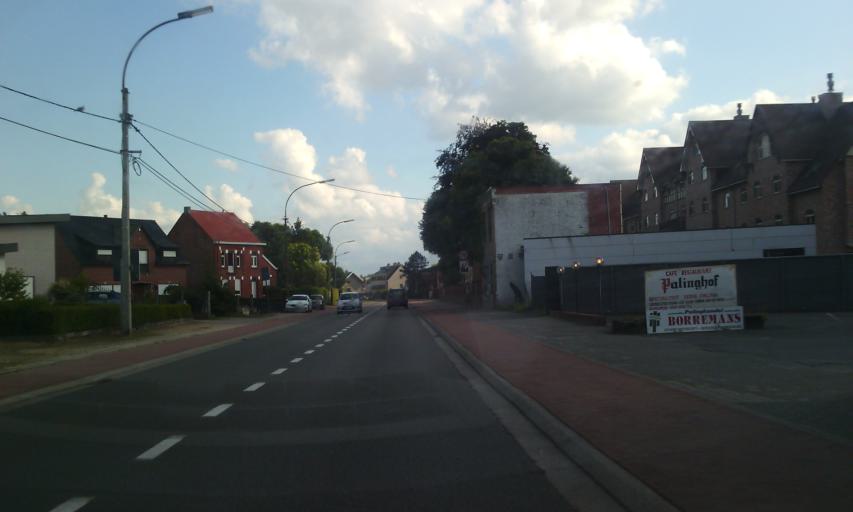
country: BE
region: Flanders
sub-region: Provincie Oost-Vlaanderen
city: Berlare
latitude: 51.0399
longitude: 3.9820
